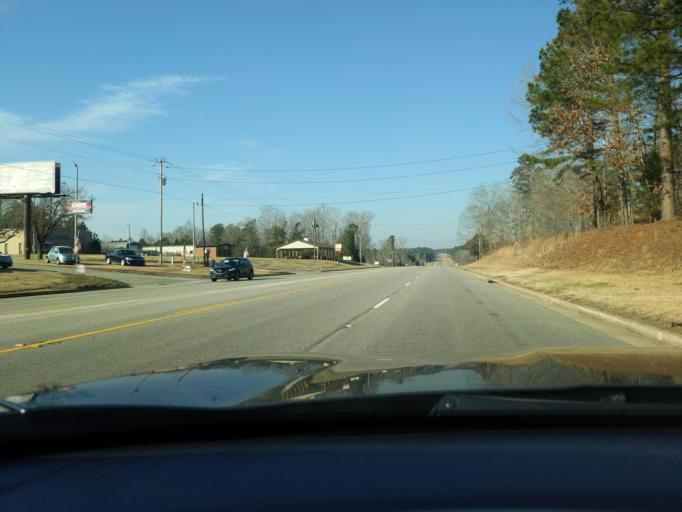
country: US
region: South Carolina
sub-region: Greenwood County
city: Greenwood
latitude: 34.1900
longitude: -82.2481
